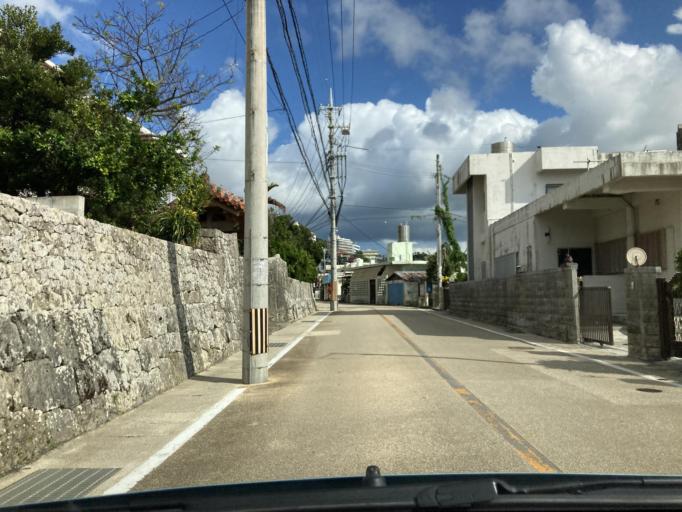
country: JP
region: Okinawa
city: Naha-shi
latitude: 26.2176
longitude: 127.7120
